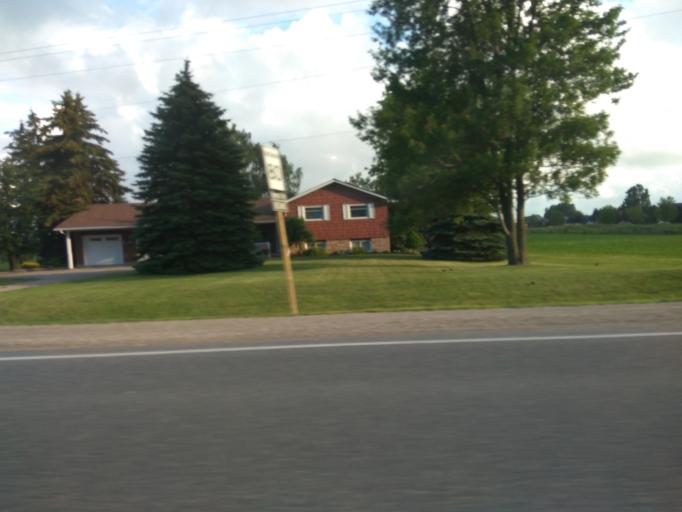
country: CA
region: Ontario
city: Stratford
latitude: 43.3695
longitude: -80.8295
